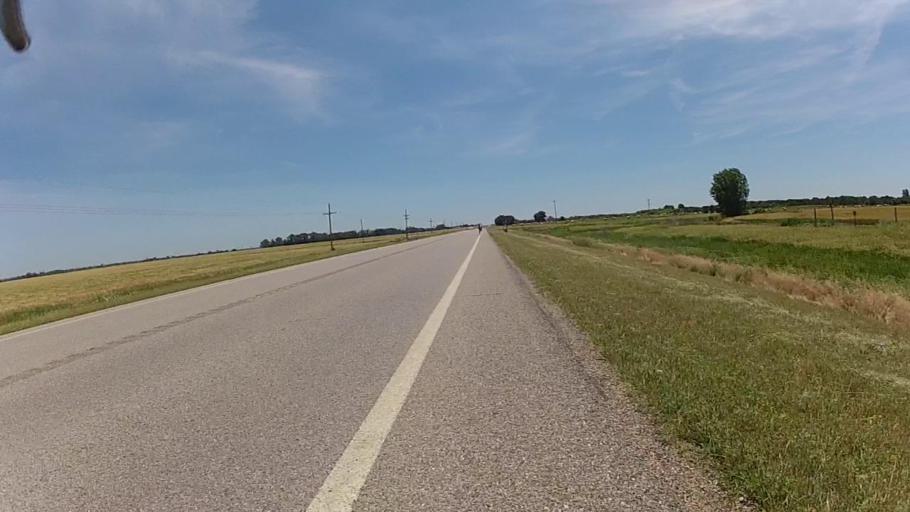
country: US
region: Kansas
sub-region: Barber County
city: Medicine Lodge
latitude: 37.2539
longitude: -98.4975
